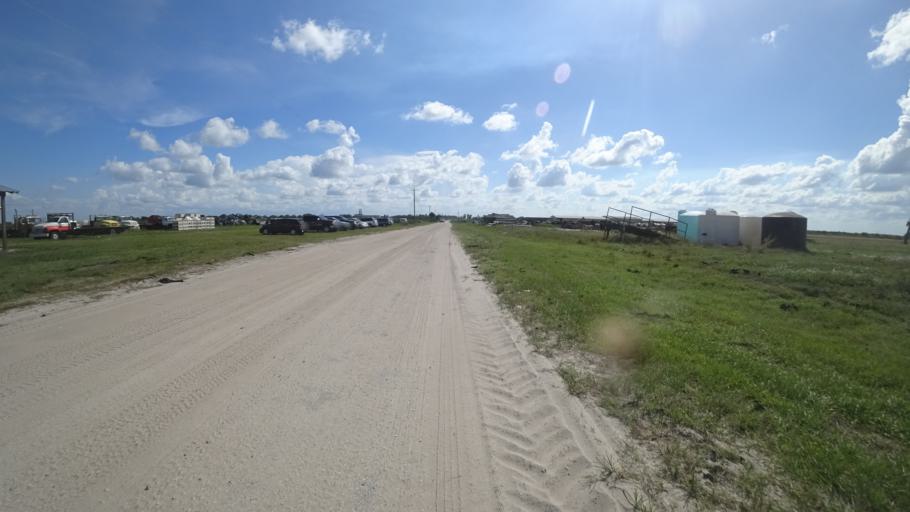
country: US
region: Florida
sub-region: DeSoto County
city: Arcadia
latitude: 27.3166
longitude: -82.1007
